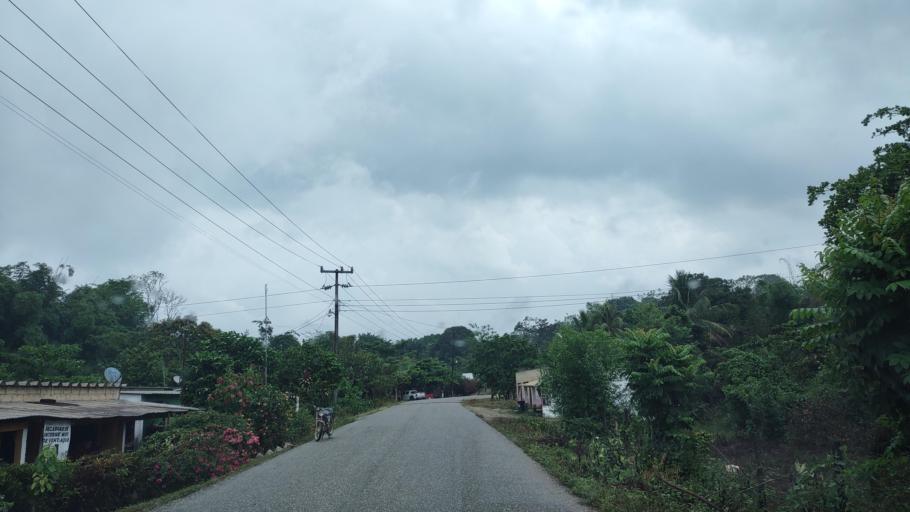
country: MX
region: Veracruz
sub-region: Uxpanapa
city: Poblado 10
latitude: 17.4734
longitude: -94.1211
